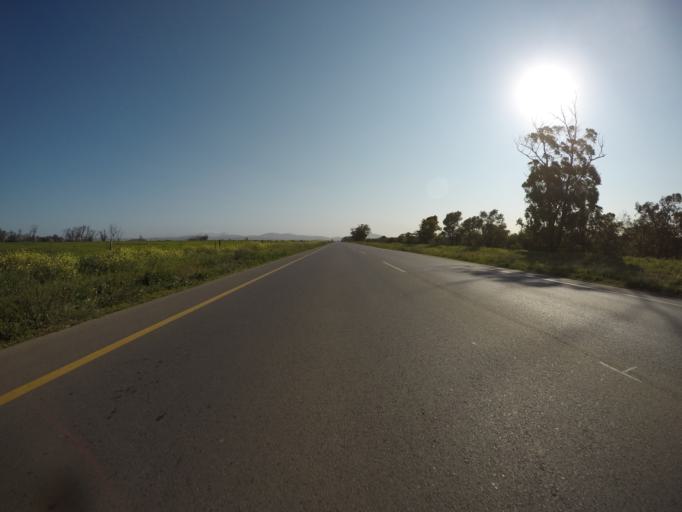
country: ZA
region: Western Cape
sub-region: City of Cape Town
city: Kraaifontein
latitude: -33.7752
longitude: 18.7439
